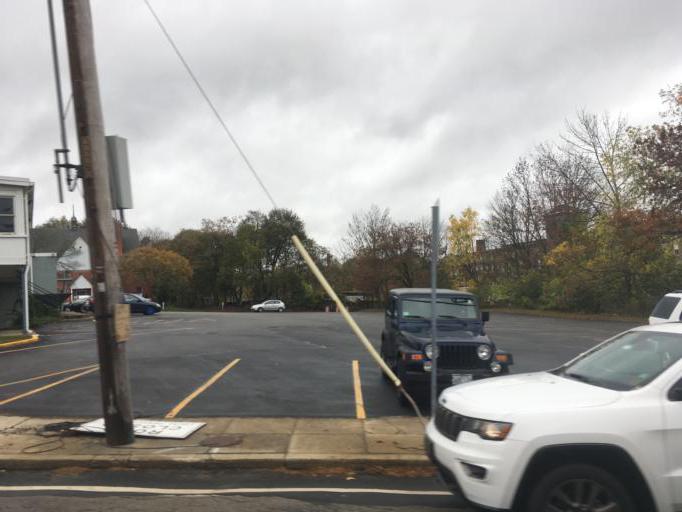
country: US
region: Rhode Island
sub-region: Kent County
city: West Warwick
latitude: 41.6962
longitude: -71.5188
